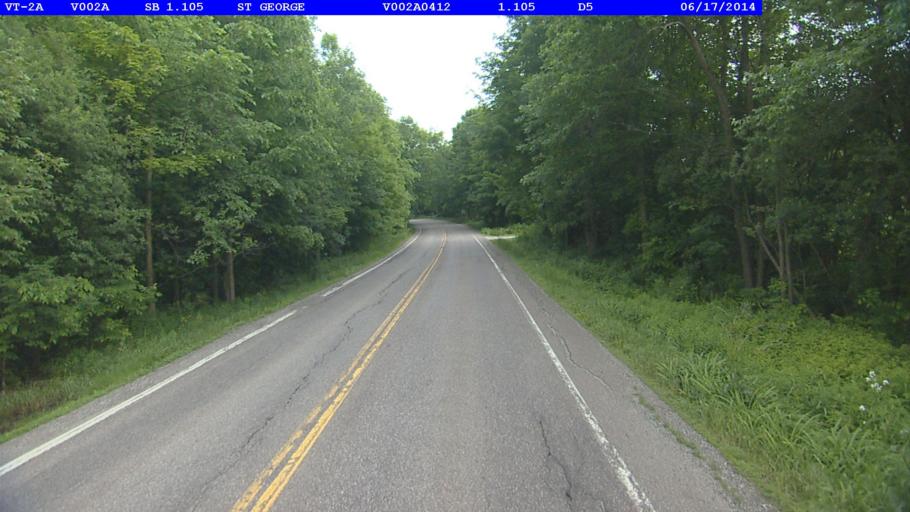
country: US
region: Vermont
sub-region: Chittenden County
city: Hinesburg
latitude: 44.3853
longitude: -73.1275
